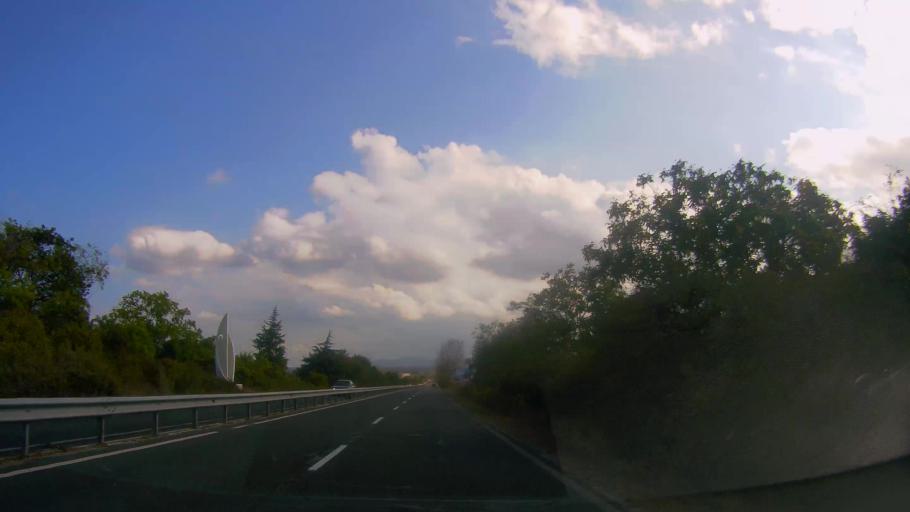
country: BG
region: Burgas
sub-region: Obshtina Sozopol
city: Chernomorets
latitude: 42.4294
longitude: 27.6397
